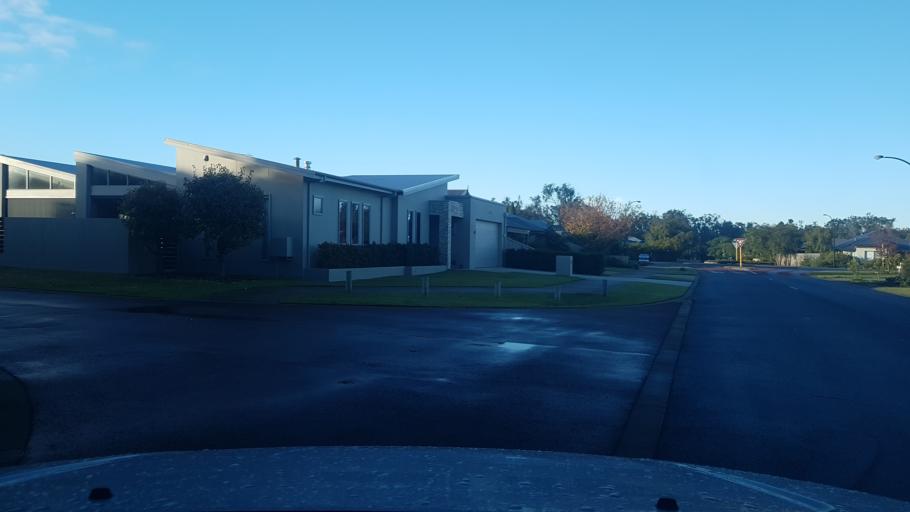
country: AU
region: Western Australia
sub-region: Busselton
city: Vasse
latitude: -33.6632
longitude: 115.2626
